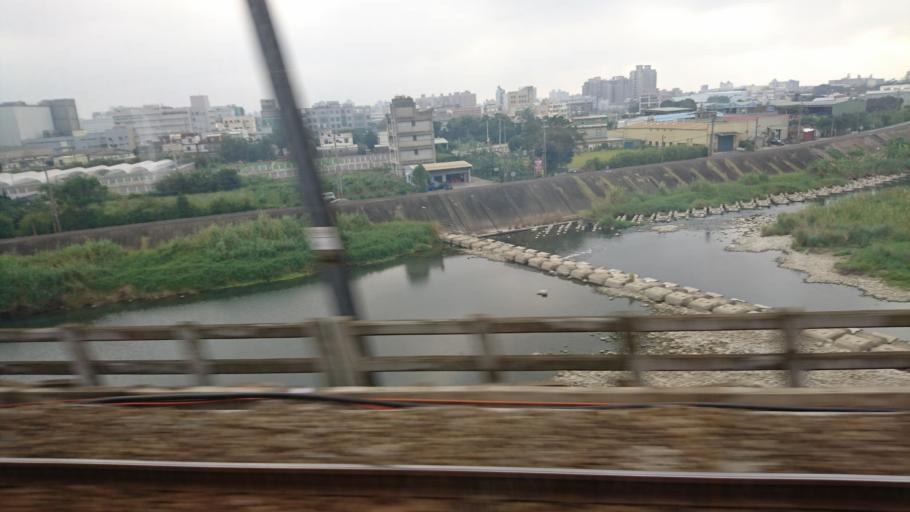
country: TW
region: Taiwan
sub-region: Hsinchu
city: Zhubei
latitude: 24.8520
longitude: 121.0123
